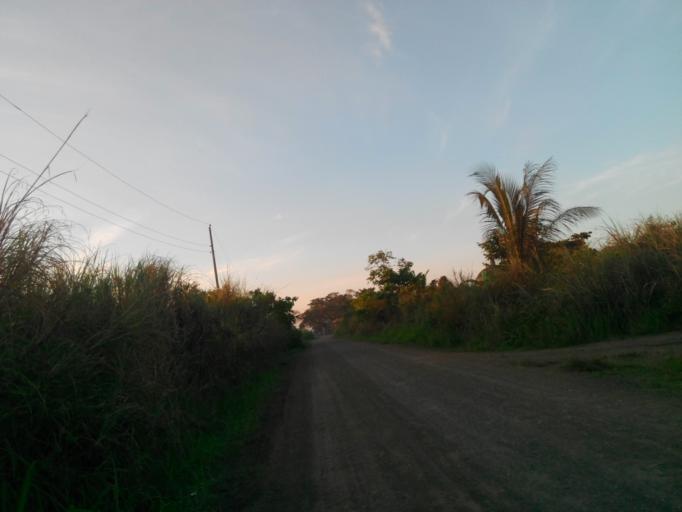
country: PH
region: Western Visayas
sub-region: Province of Iloilo
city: Passi
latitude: 11.1194
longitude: 122.6470
